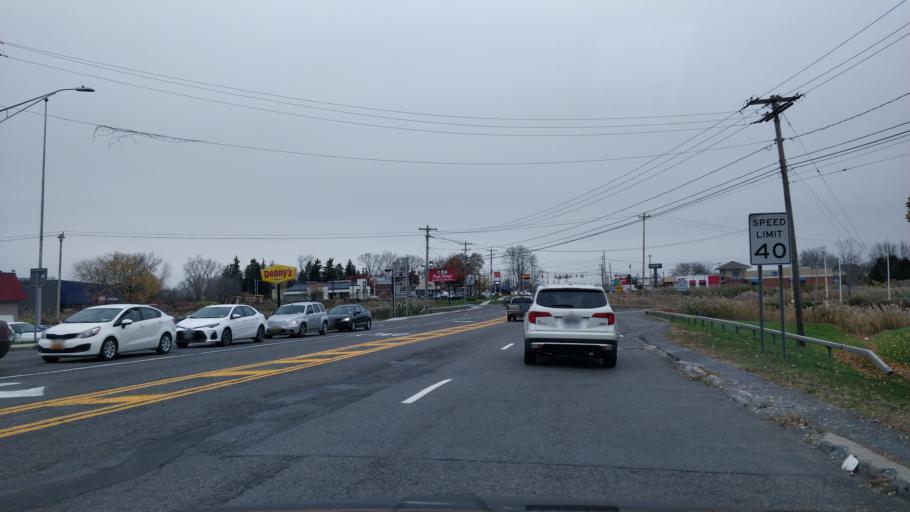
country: US
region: New York
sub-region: Onondaga County
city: North Syracuse
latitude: 43.1500
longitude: -76.1253
